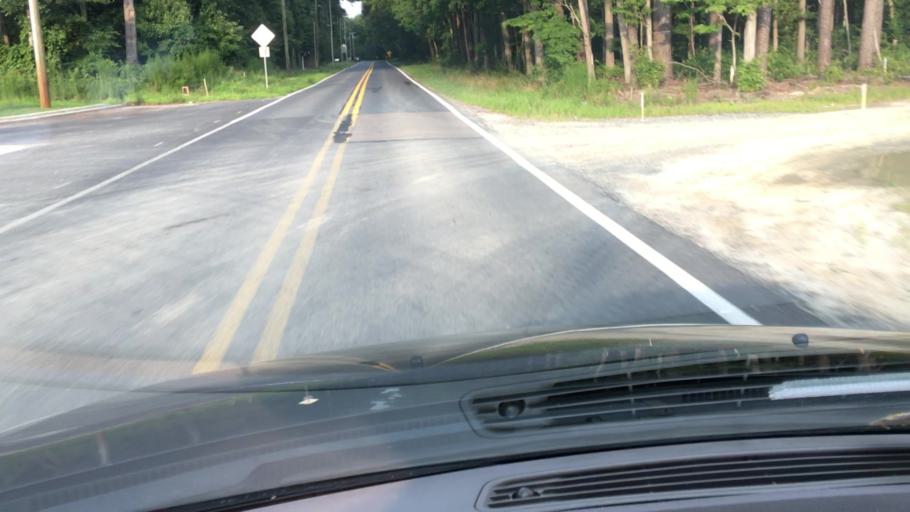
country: US
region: Delaware
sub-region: Sussex County
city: Ocean View
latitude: 38.5065
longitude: -75.1197
